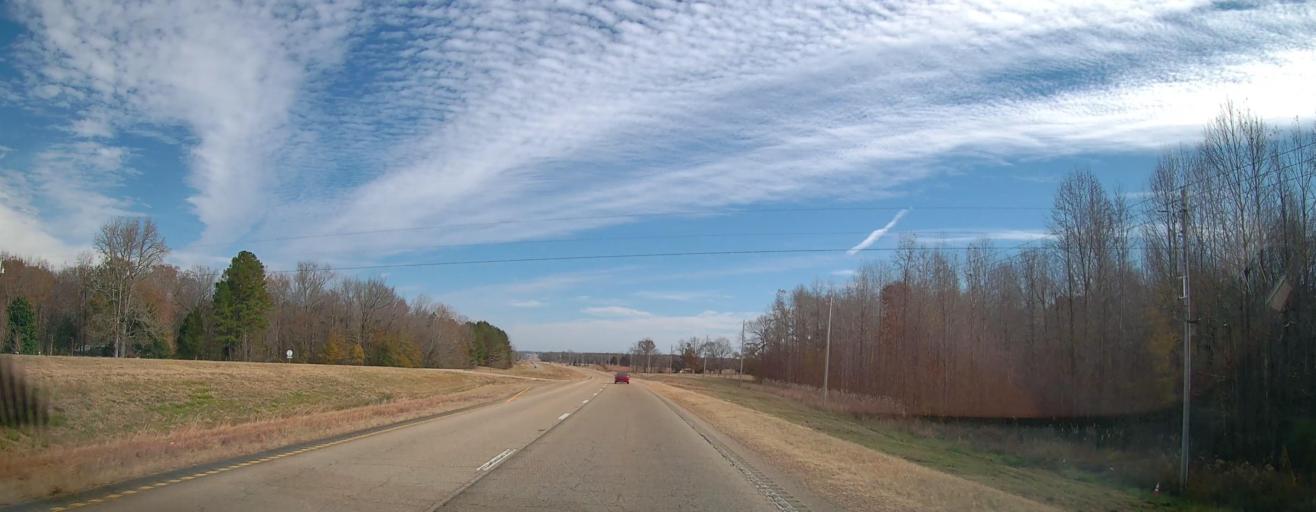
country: US
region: Mississippi
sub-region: Alcorn County
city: Corinth
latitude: 34.9312
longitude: -88.6404
